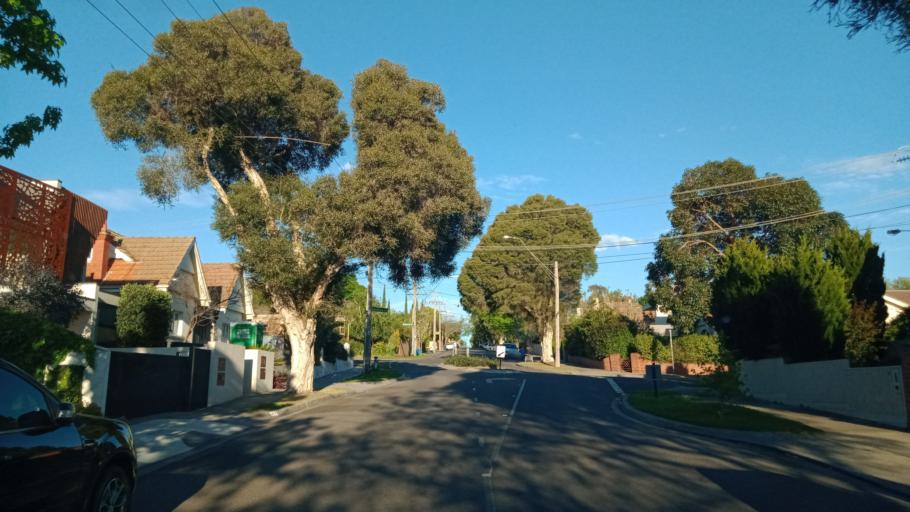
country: AU
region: Victoria
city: Glenferrie
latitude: -37.8347
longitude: 145.0515
